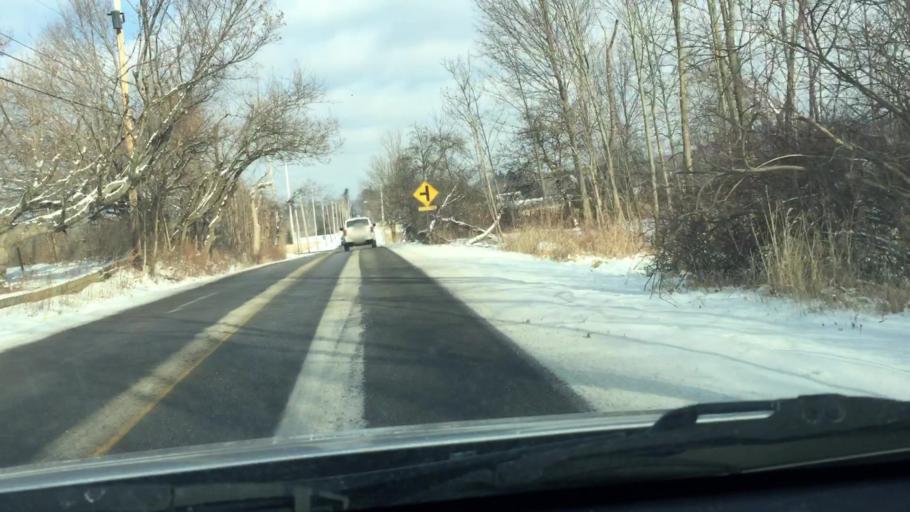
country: US
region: Ohio
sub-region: Mahoning County
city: Boardman
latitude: 41.0059
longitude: -80.7113
